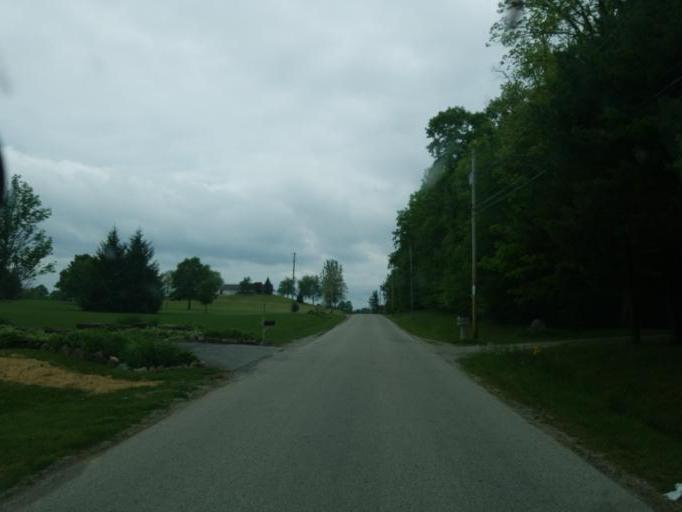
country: US
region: Ohio
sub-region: Richland County
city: Lexington
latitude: 40.6562
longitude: -82.6230
